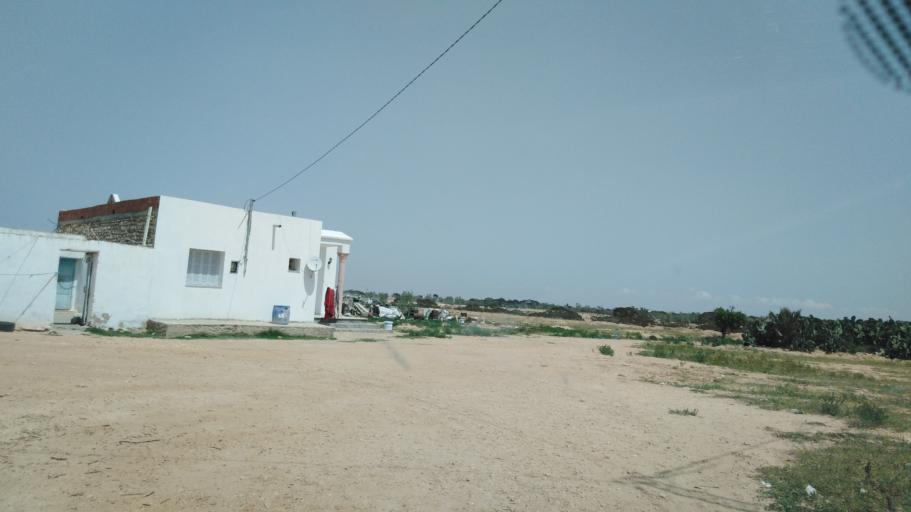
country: TN
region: Safaqis
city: Sfax
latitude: 34.7215
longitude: 10.5667
